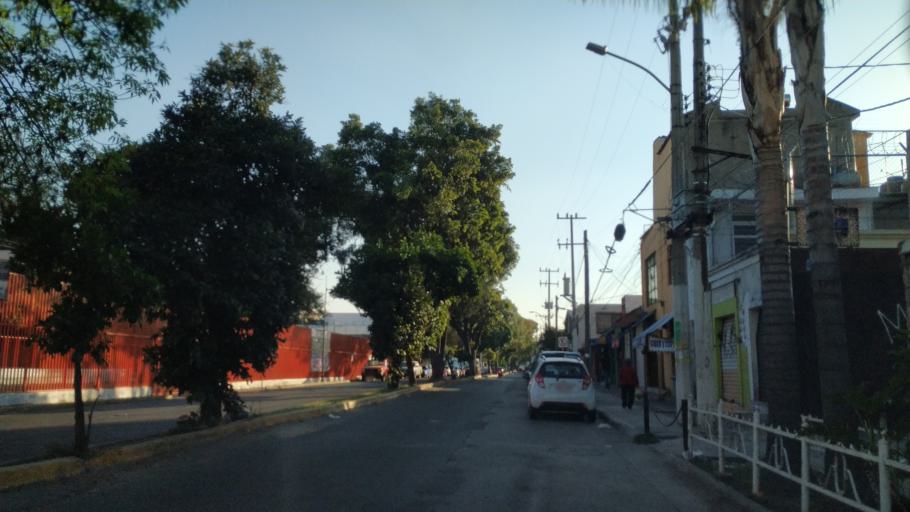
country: MX
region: Jalisco
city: Tlaquepaque
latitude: 20.6607
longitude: -103.3264
